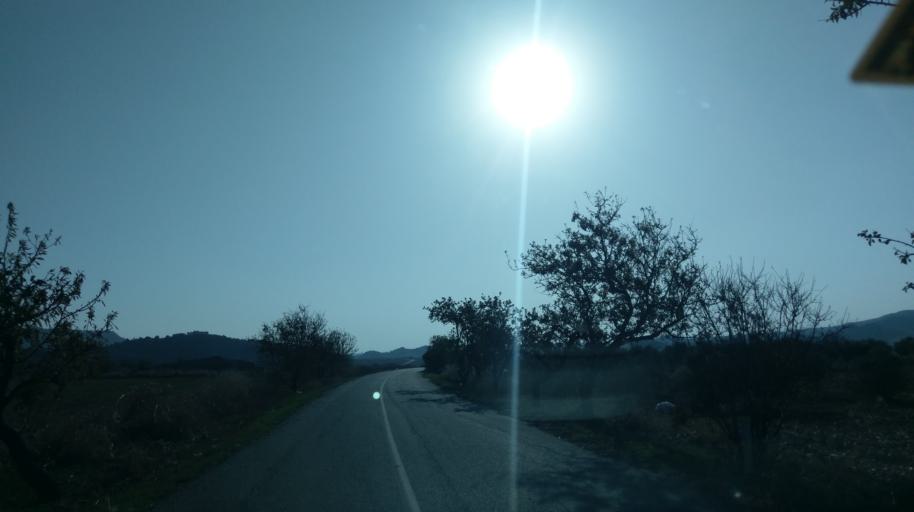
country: CY
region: Ammochostos
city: Leonarisso
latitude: 35.4704
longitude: 34.1040
